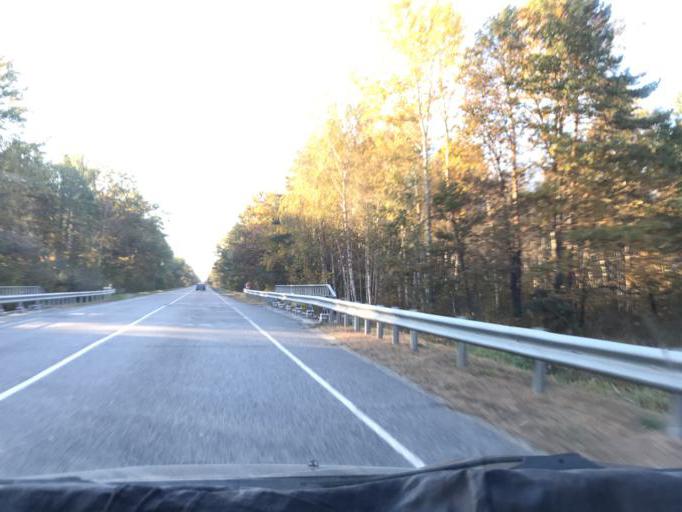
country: BY
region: Gomel
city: Pyetrykaw
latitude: 52.2602
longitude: 28.3300
